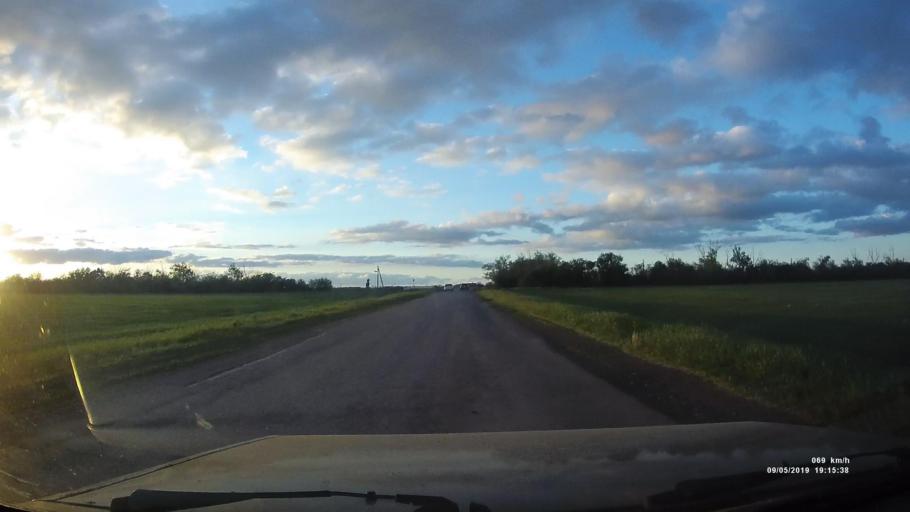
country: RU
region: Krasnodarskiy
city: Kanelovskaya
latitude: 46.7697
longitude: 39.2113
